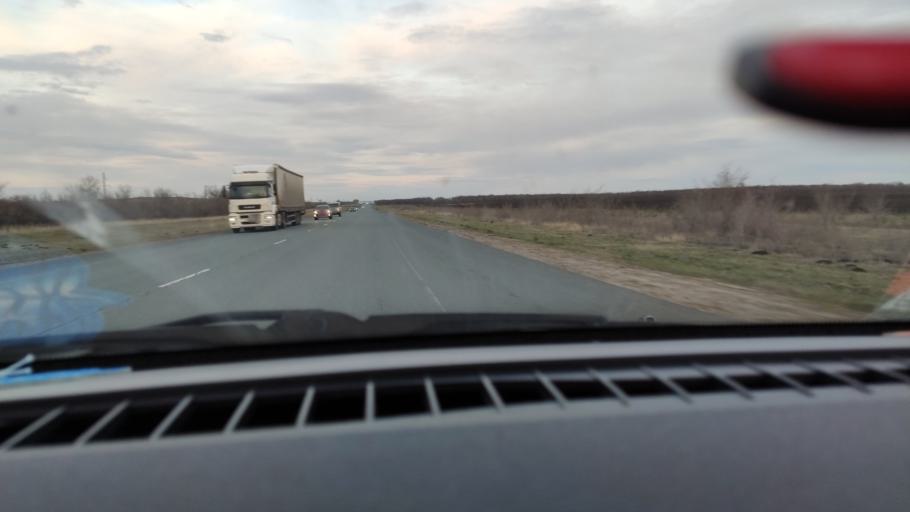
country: RU
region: Saratov
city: Yelshanka
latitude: 51.8281
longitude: 46.2624
